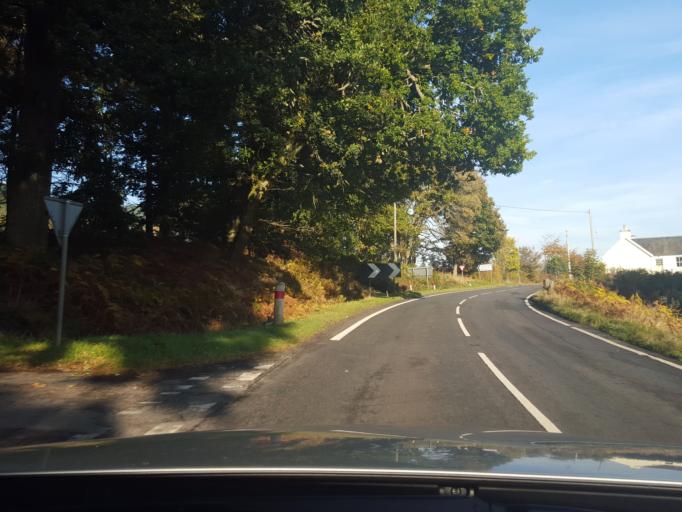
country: GB
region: Scotland
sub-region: Highland
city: Inverness
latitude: 57.4440
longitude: -4.2950
